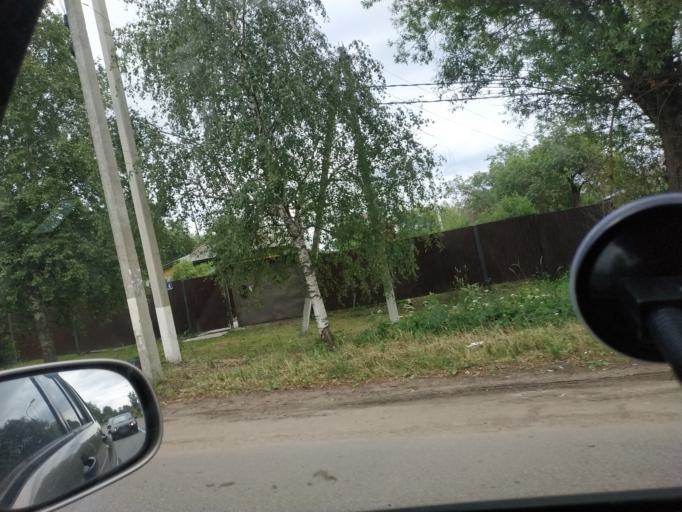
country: RU
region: Moskovskaya
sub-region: Shchelkovskiy Rayon
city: Grebnevo
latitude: 55.9815
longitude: 38.1190
